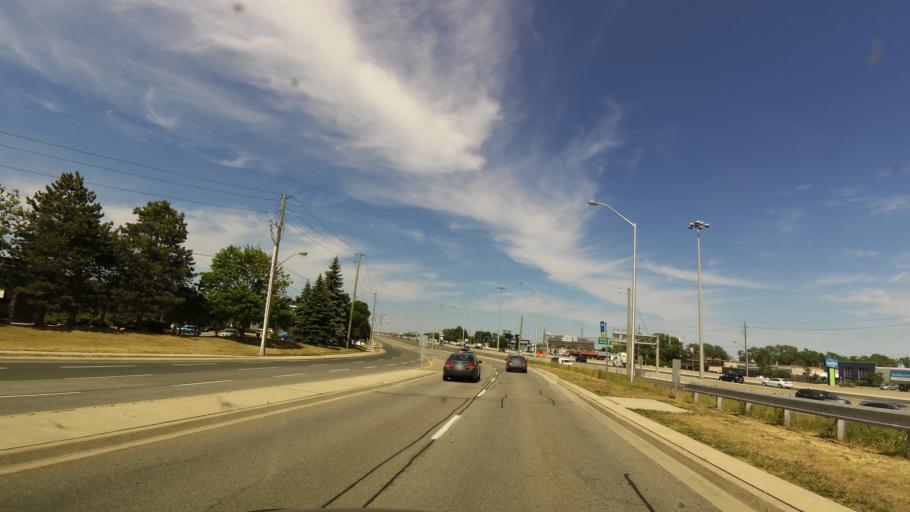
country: CA
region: Ontario
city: Oakville
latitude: 43.4397
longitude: -79.7087
